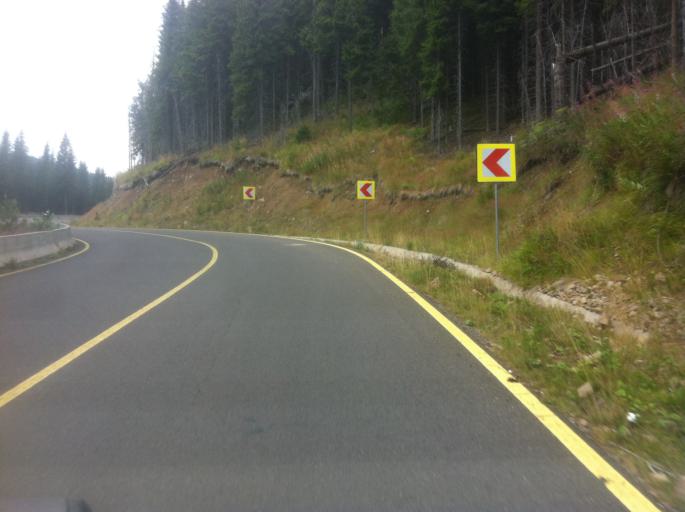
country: RO
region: Hunedoara
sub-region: Oras Petrila
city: Petrila
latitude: 45.4546
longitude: 23.6154
